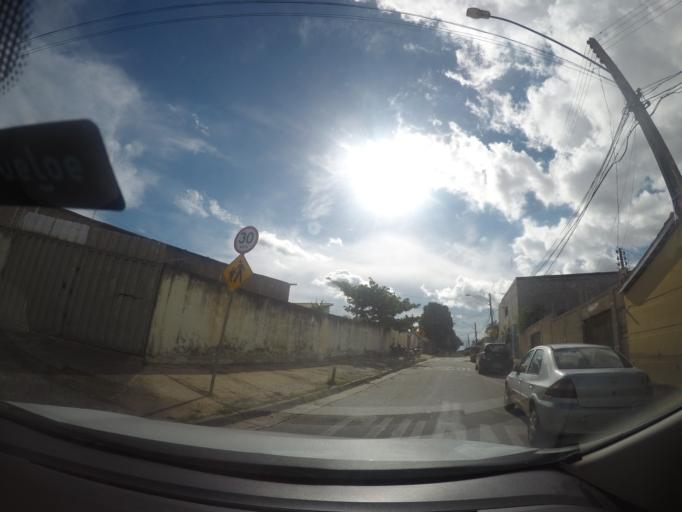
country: BR
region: Goias
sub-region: Goiania
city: Goiania
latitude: -16.6800
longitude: -49.3051
